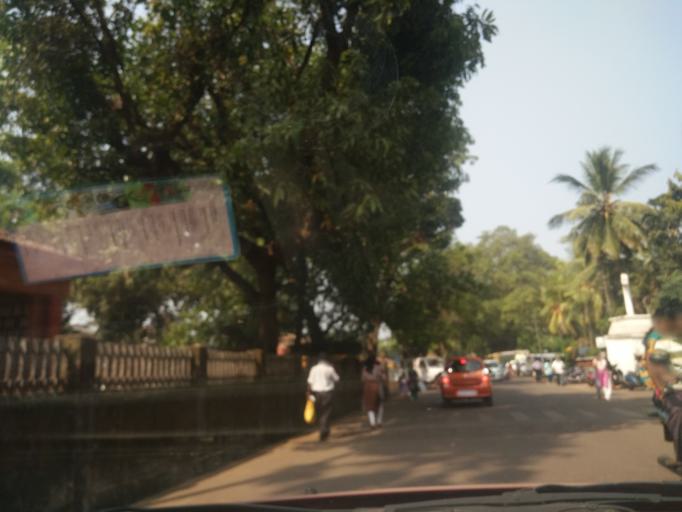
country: IN
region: Goa
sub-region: North Goa
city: Dicholi
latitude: 15.5886
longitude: 73.9476
